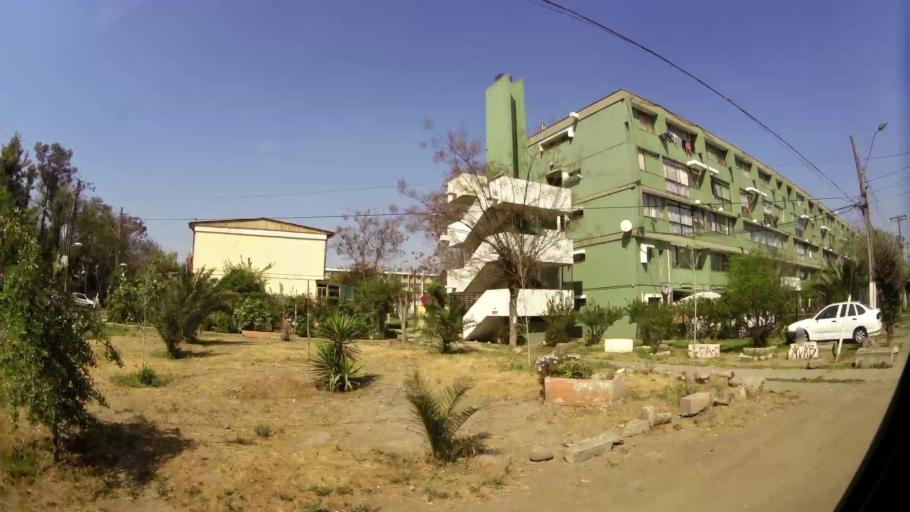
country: CL
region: Santiago Metropolitan
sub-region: Provincia de Santiago
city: Lo Prado
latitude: -33.4465
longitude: -70.6867
